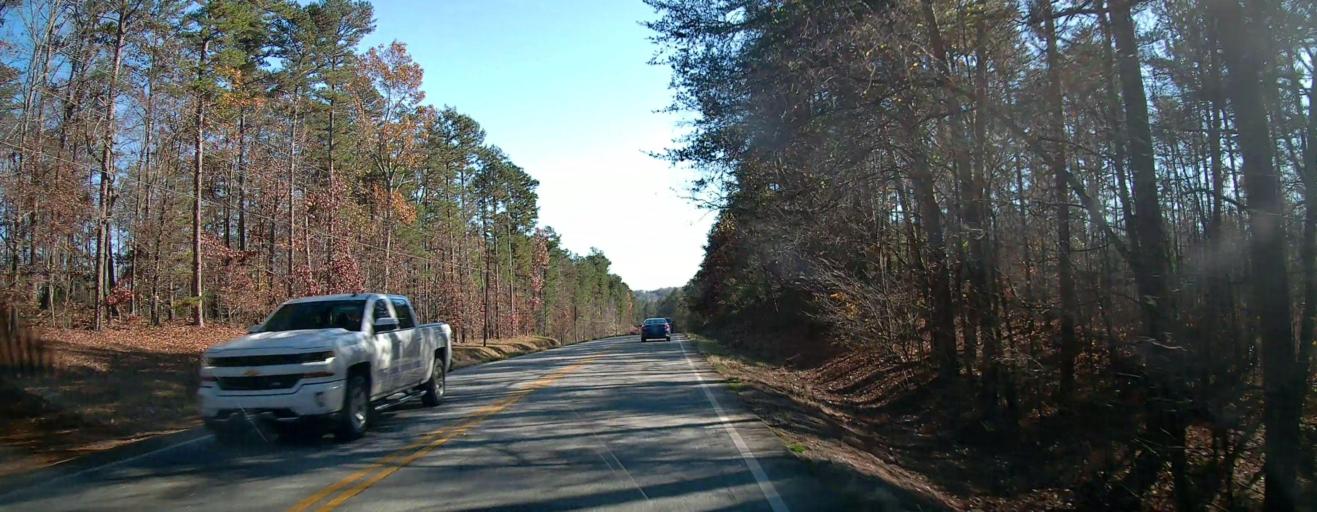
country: US
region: Georgia
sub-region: Hall County
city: Lula
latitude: 34.4266
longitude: -83.7123
